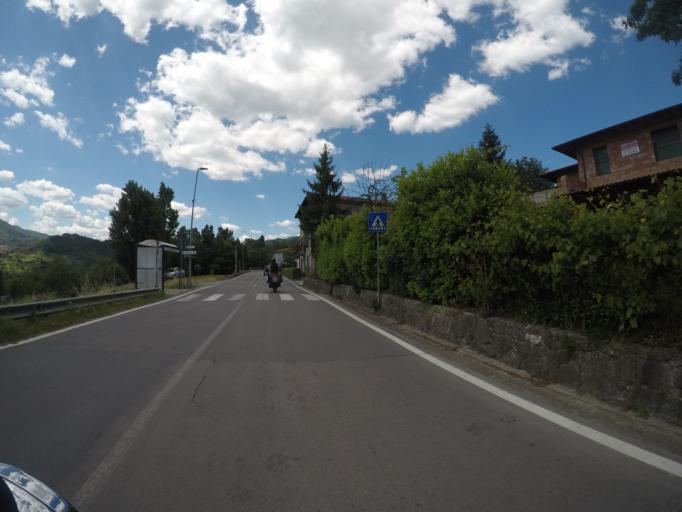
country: IT
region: Tuscany
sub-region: Provincia di Lucca
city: Villa Collemandina
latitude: 44.1449
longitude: 10.3734
